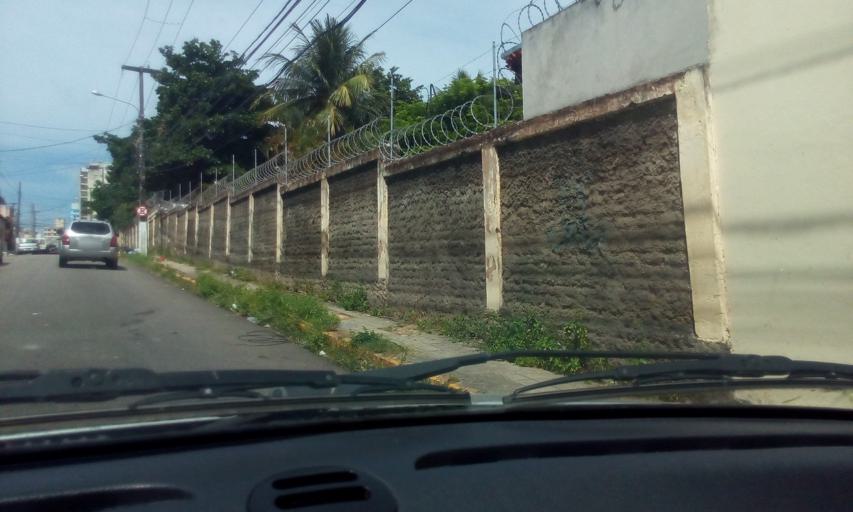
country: BR
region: Rio Grande do Norte
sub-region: Natal
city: Natal
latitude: -5.7920
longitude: -35.2065
